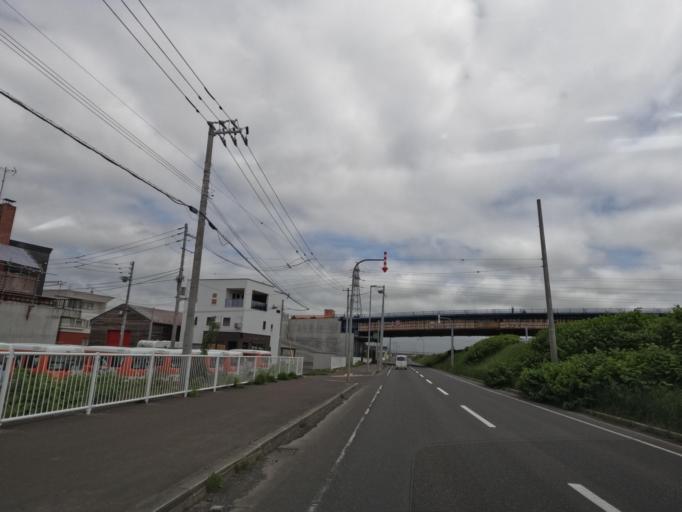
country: JP
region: Hokkaido
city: Sapporo
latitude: 43.0816
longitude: 141.4115
